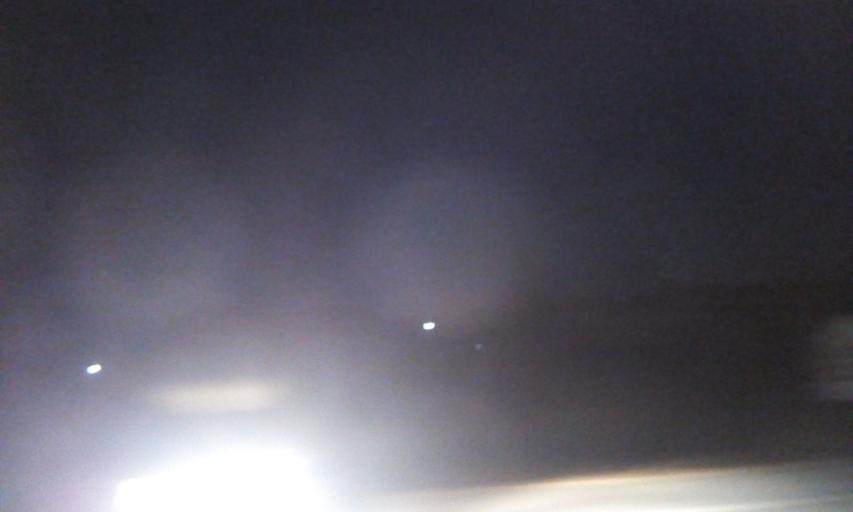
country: TH
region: Sing Buri
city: Sing Buri
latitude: 14.8628
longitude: 100.4412
